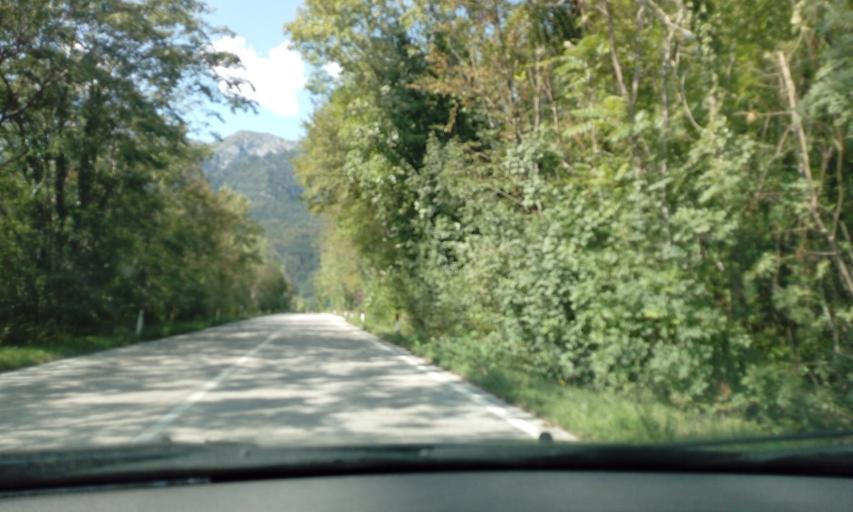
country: IT
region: Friuli Venezia Giulia
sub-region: Provincia di Udine
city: Trasaghis
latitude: 46.3066
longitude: 13.0595
